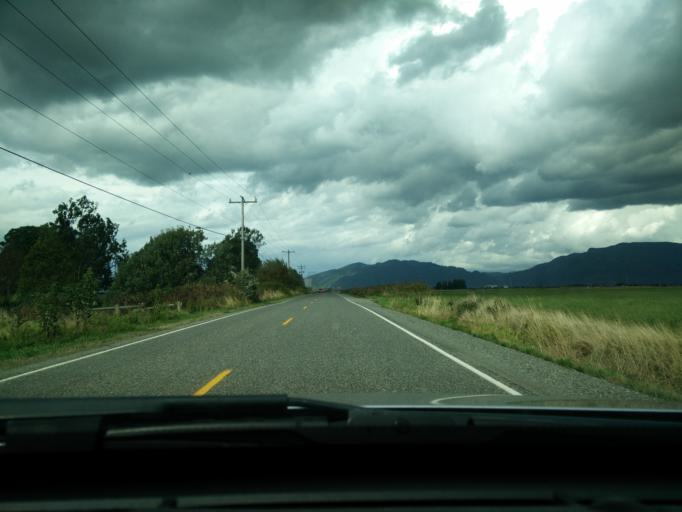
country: US
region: Washington
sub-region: Skagit County
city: Anacortes
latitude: 48.5442
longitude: -122.4720
